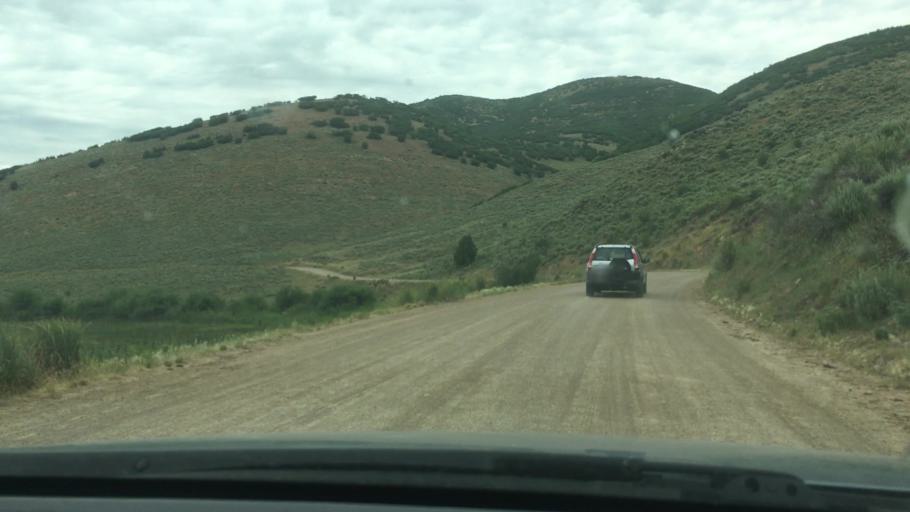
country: US
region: Utah
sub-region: Summit County
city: Summit Park
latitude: 40.7775
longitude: -111.5881
